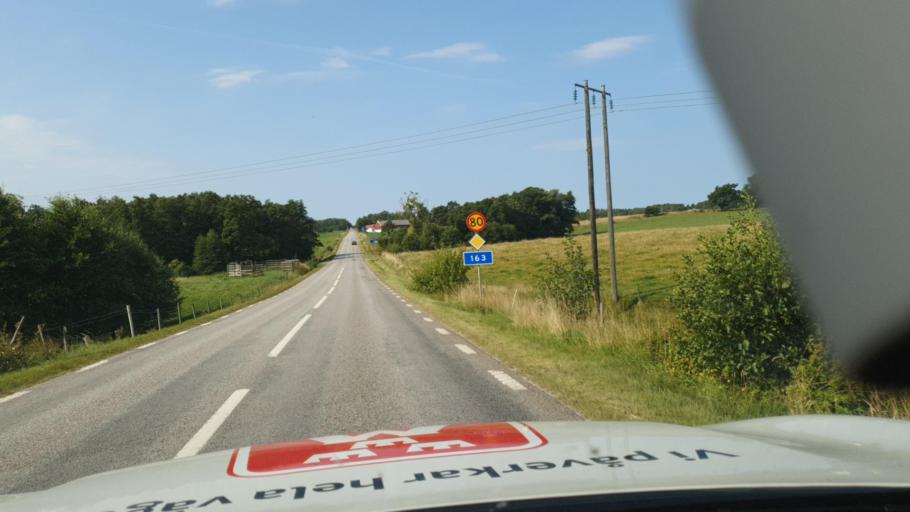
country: SE
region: Vaestra Goetaland
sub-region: Tanums Kommun
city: Tanumshede
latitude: 58.7216
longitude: 11.3716
